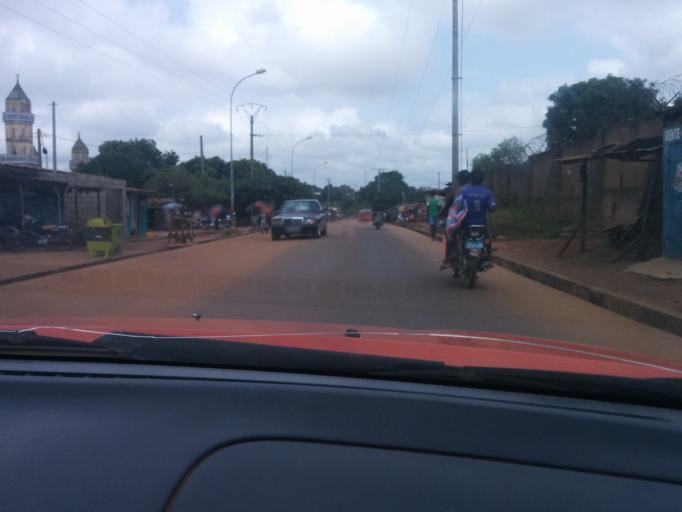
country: CI
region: Vallee du Bandama
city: Bouake
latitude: 7.6967
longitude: -5.0369
